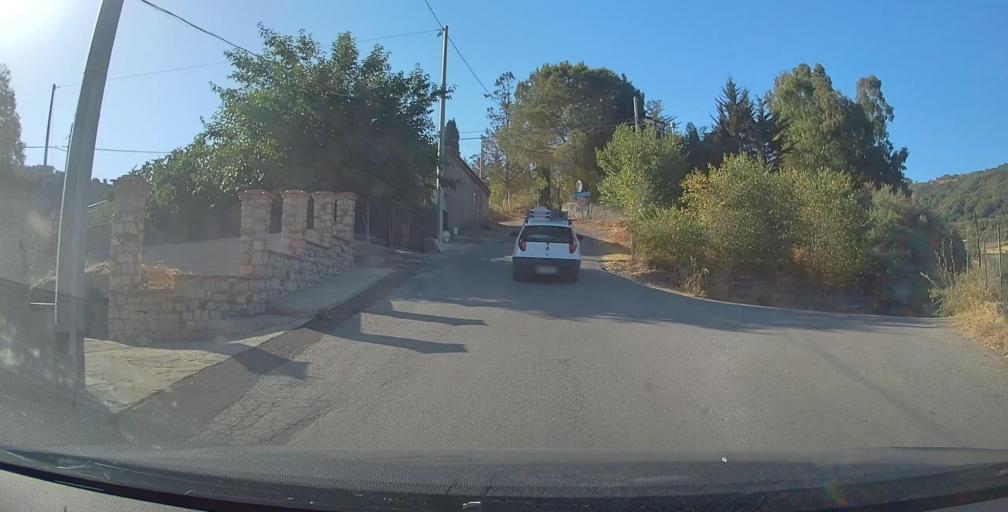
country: IT
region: Sicily
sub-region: Messina
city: San Piero Patti
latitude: 38.0589
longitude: 14.9934
